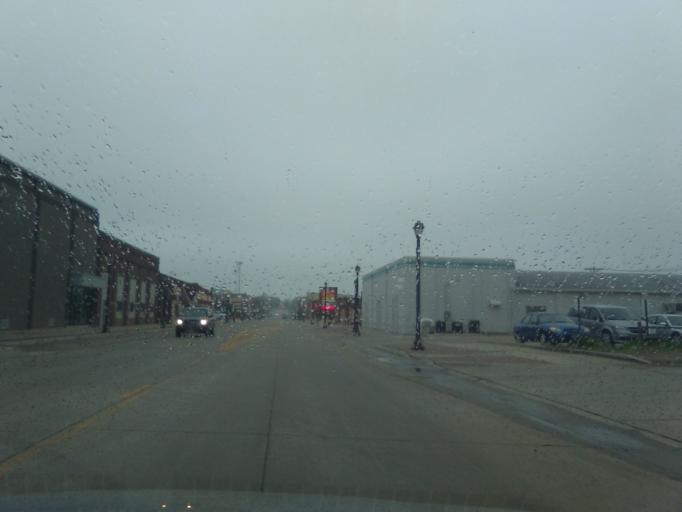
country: US
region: Nebraska
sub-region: Wayne County
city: Wayne
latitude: 42.2273
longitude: -97.0177
